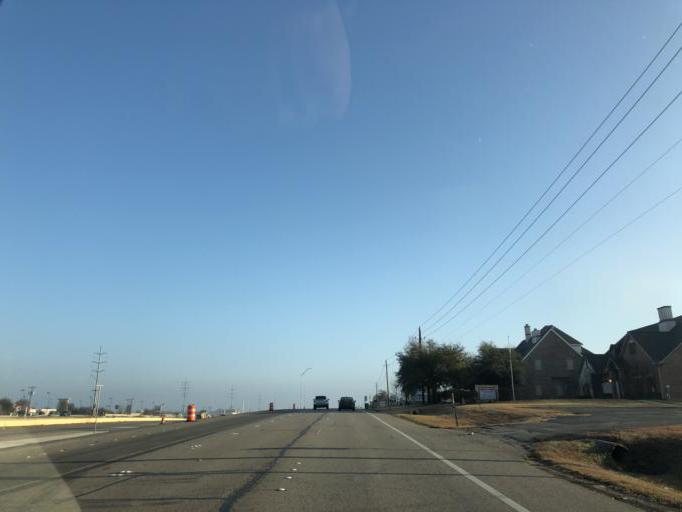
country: US
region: Texas
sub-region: Dallas County
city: Cedar Hill
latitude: 32.6003
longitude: -96.9347
